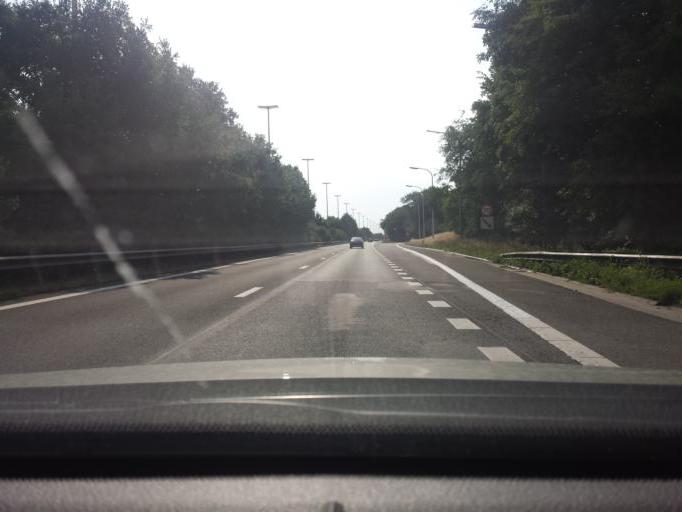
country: BE
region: Flanders
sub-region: Provincie Limburg
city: Diepenbeek
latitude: 50.8963
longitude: 5.3967
